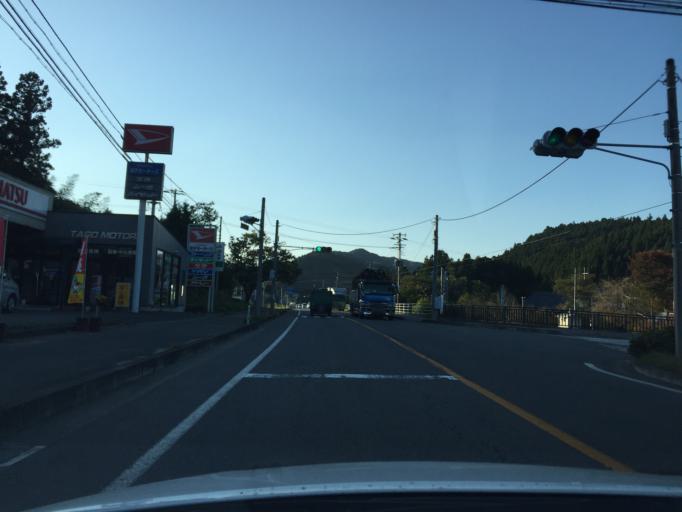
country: JP
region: Fukushima
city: Iwaki
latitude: 37.1413
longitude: 140.6876
